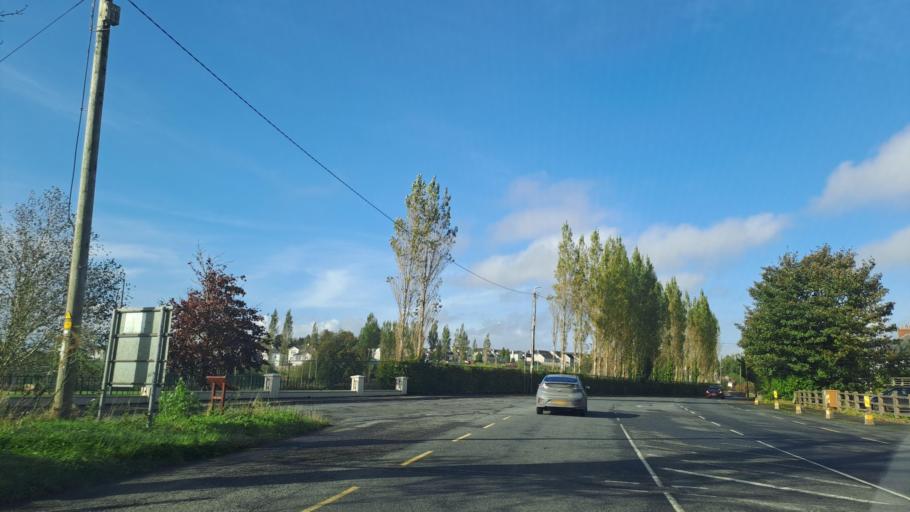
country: IE
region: Ulster
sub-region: An Cabhan
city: Cootehill
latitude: 54.0674
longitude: -7.0632
